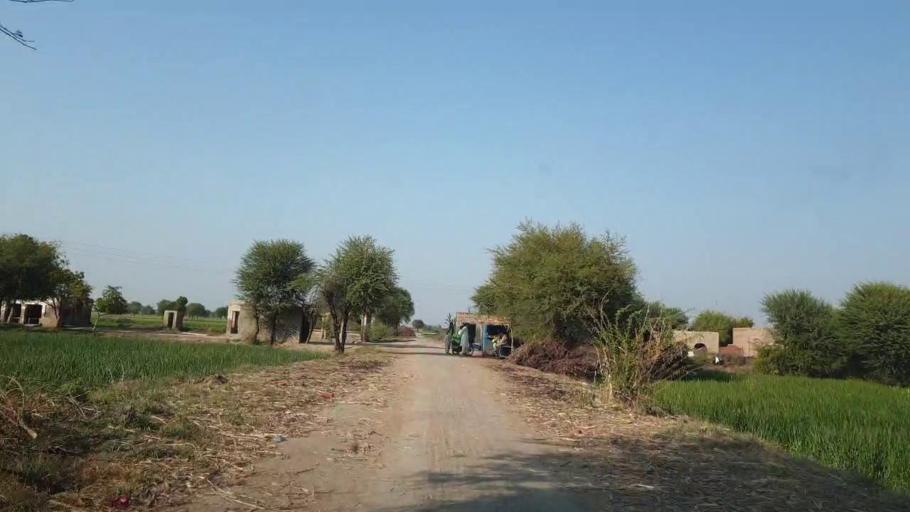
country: PK
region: Sindh
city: Tando Mittha Khan
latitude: 25.7564
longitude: 69.2046
